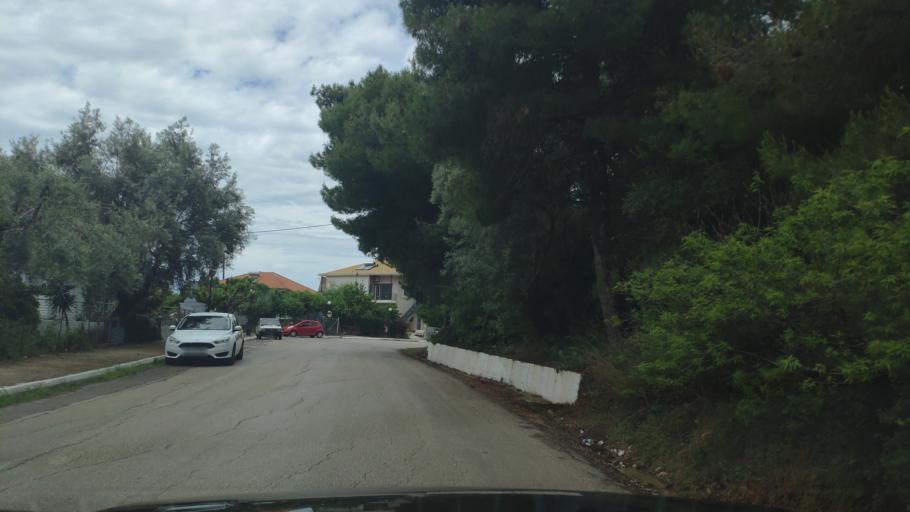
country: GR
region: West Greece
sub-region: Nomos Aitolias kai Akarnanias
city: Palairos
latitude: 38.7793
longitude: 20.8848
